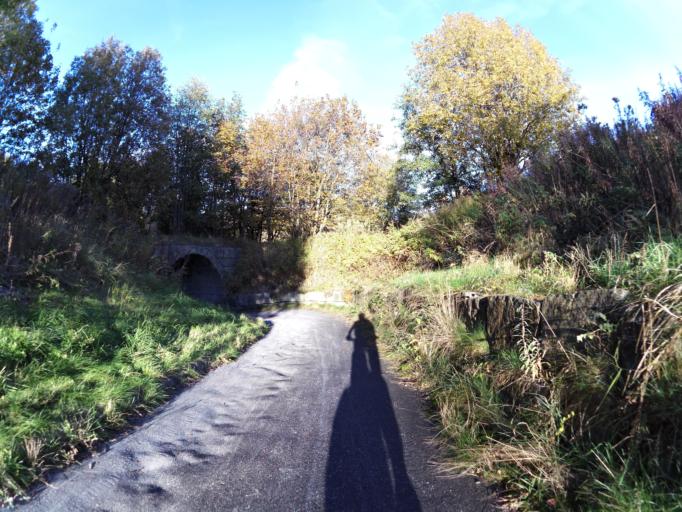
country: NO
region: Ostfold
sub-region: Sarpsborg
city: Sarpsborg
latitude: 59.2614
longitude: 11.1131
